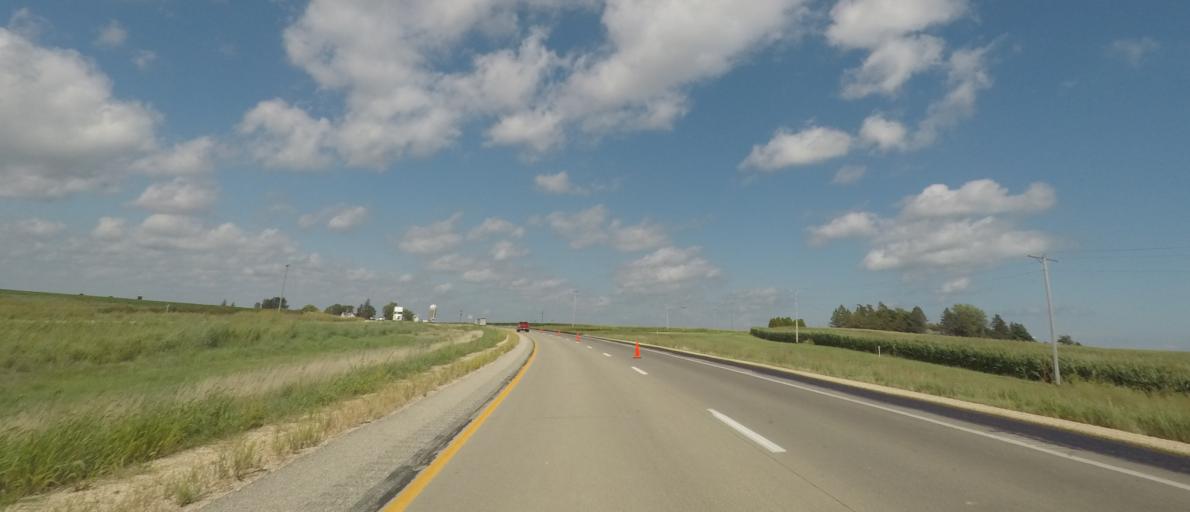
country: US
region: Iowa
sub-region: Jones County
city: Anamosa
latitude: 42.1420
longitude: -91.2414
